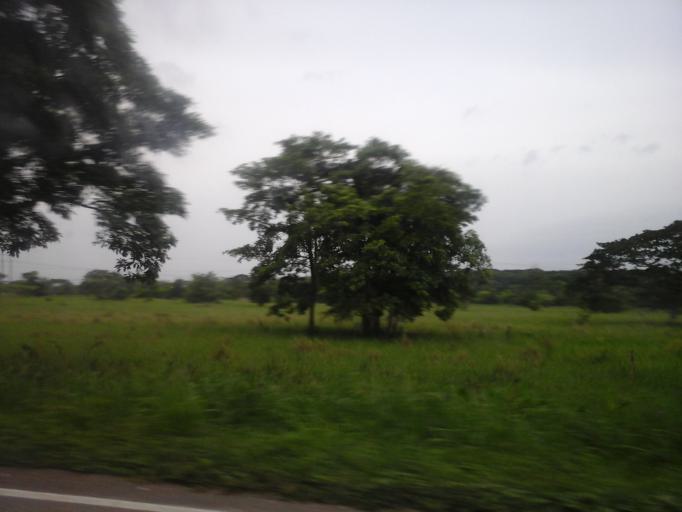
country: CO
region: Bolivar
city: San Pablo
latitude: 10.1363
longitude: -75.2661
